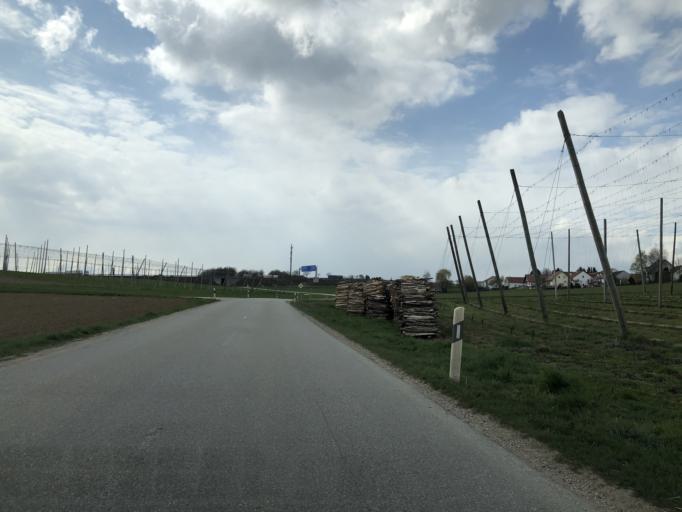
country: DE
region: Bavaria
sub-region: Upper Bavaria
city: Schweitenkirchen
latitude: 48.4994
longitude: 11.5995
